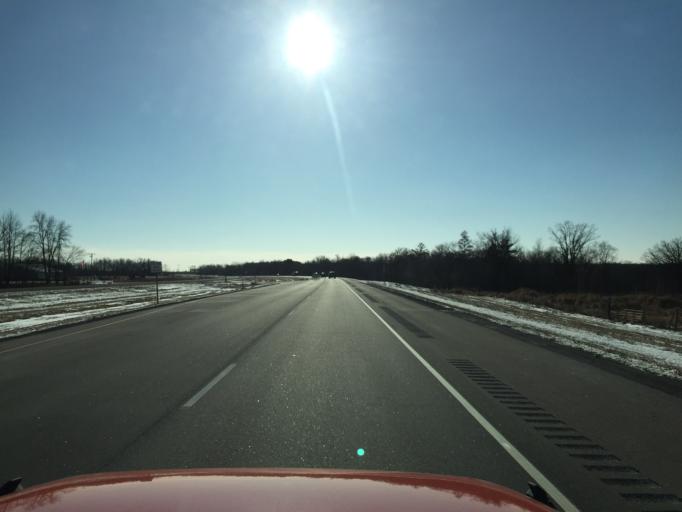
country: US
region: Minnesota
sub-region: Mille Lacs County
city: Milaca
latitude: 45.8344
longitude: -93.6614
